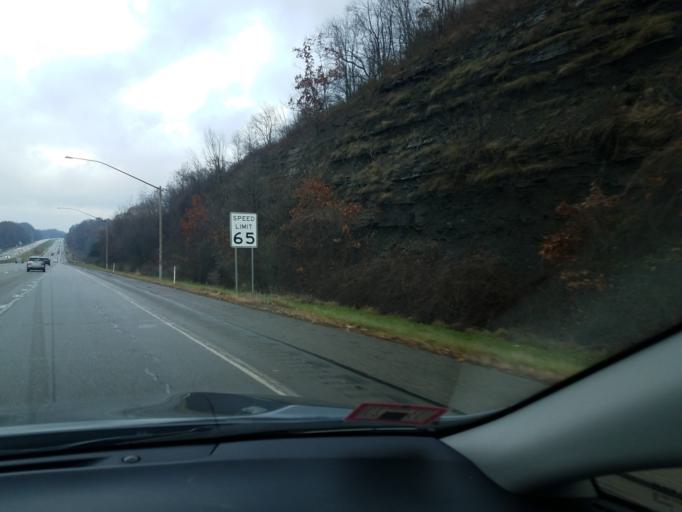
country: US
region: Pennsylvania
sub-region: Allegheny County
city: Bradford Woods
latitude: 40.6199
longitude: -80.0957
